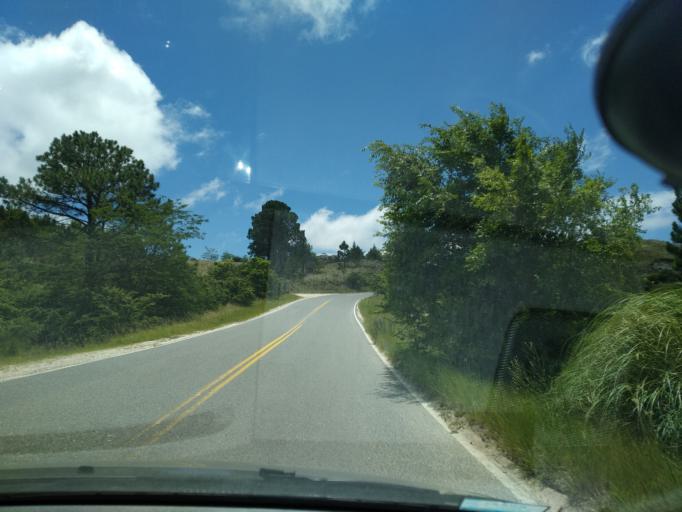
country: AR
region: Cordoba
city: Cuesta Blanca
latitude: -31.5972
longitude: -64.5438
